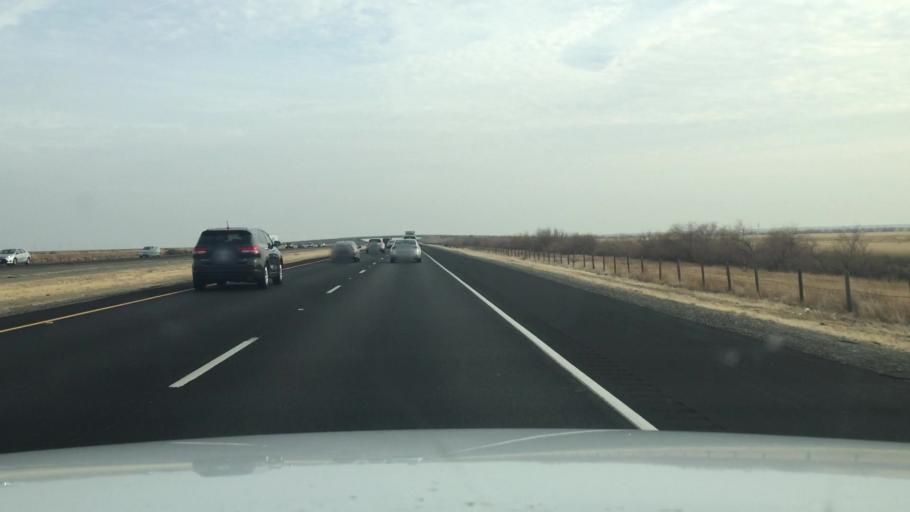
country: US
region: California
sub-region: Kern County
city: Lost Hills
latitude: 35.7100
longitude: -119.7233
